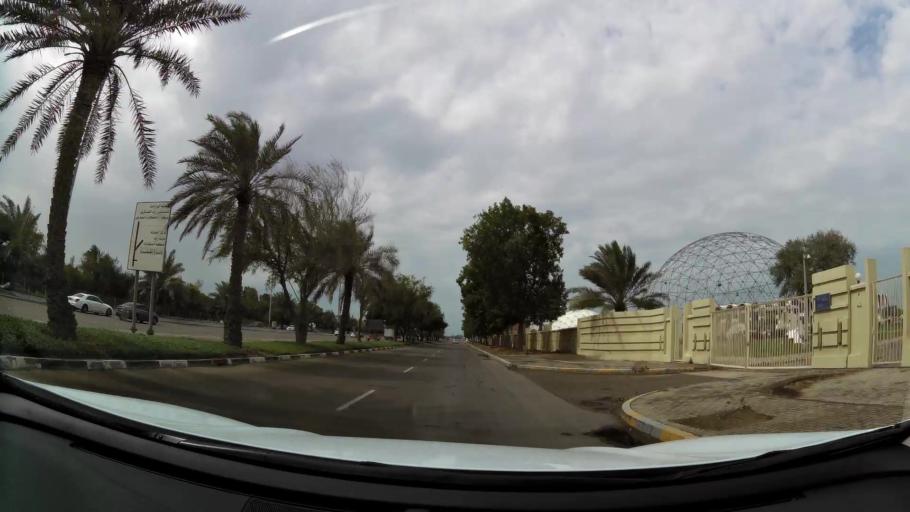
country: AE
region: Abu Dhabi
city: Abu Dhabi
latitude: 24.4121
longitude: 54.4560
